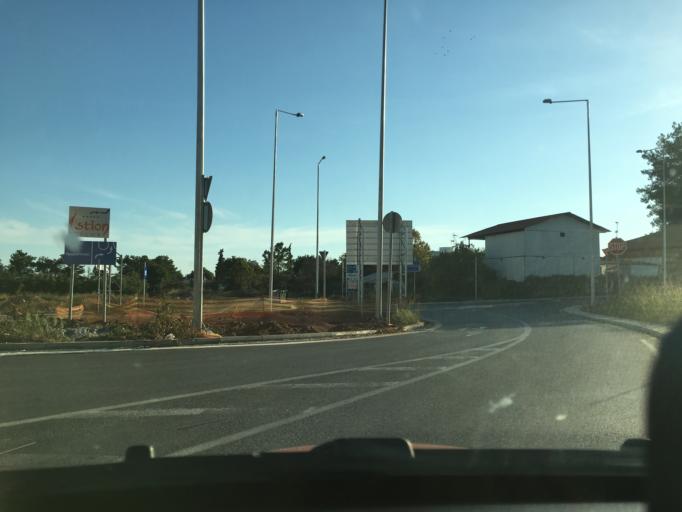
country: GR
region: Central Macedonia
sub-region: Nomos Chalkidikis
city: Nea Poteidaia
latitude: 40.2251
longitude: 23.3137
